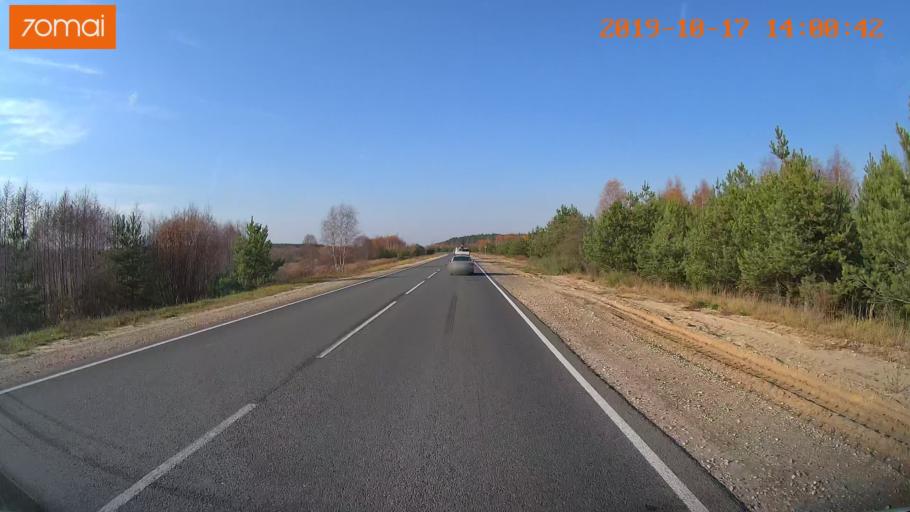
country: RU
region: Rjazan
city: Spas-Klepiki
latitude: 55.1478
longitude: 40.1761
